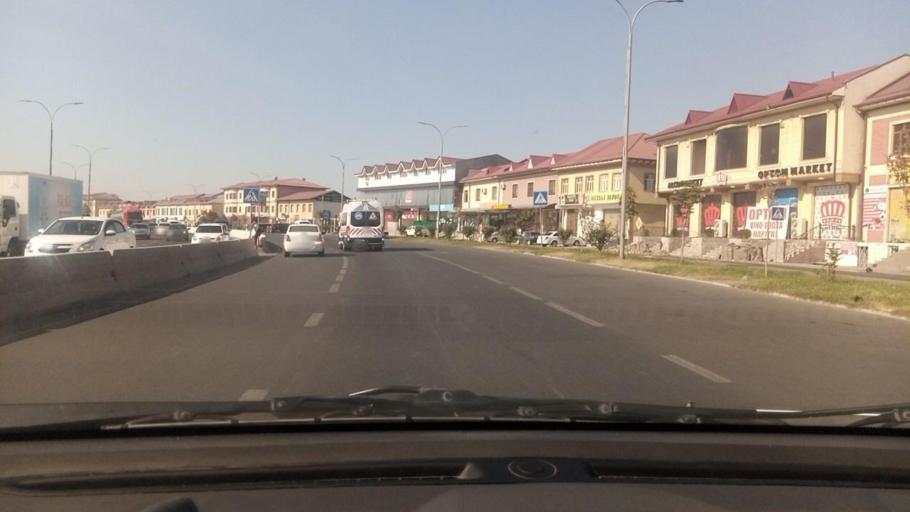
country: UZ
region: Toshkent Shahri
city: Bektemir
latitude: 41.2243
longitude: 69.3343
